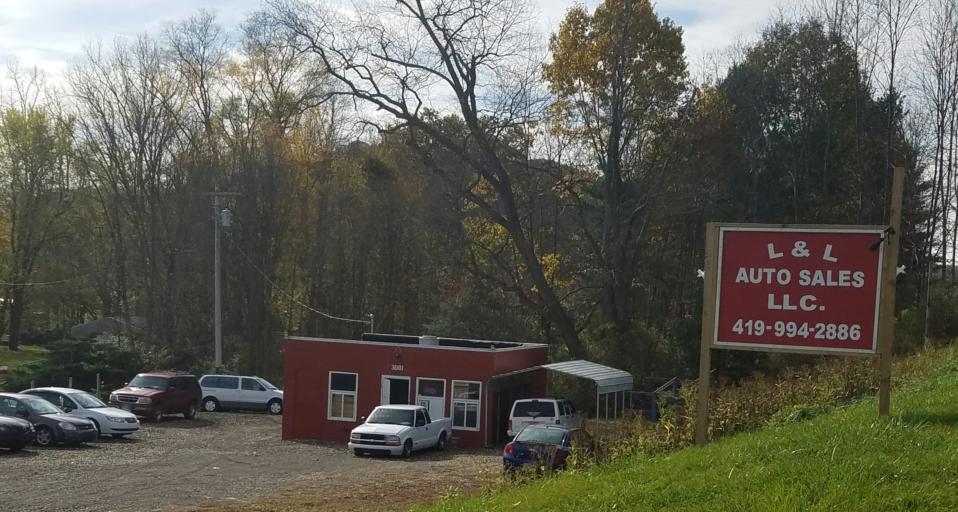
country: US
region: Ohio
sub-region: Ashland County
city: Loudonville
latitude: 40.6145
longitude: -82.2547
